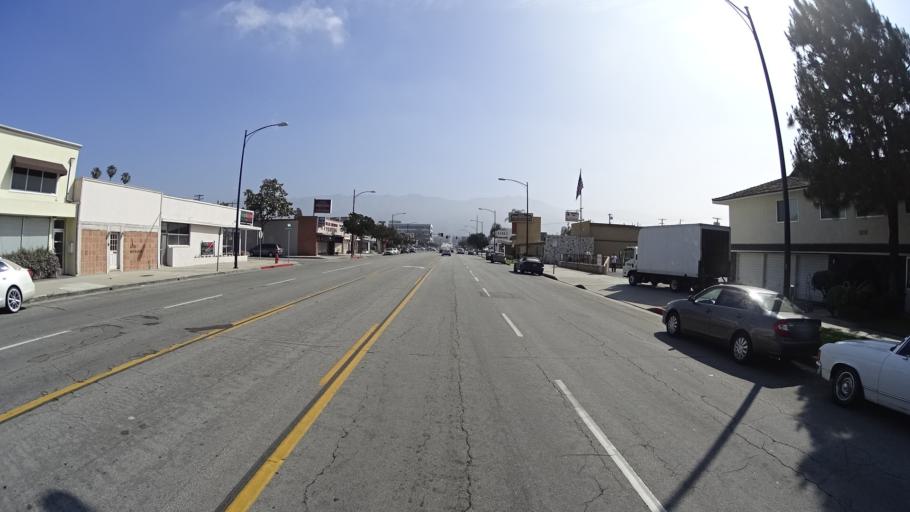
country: US
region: California
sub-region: Los Angeles County
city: Burbank
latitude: 34.1722
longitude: -118.3178
